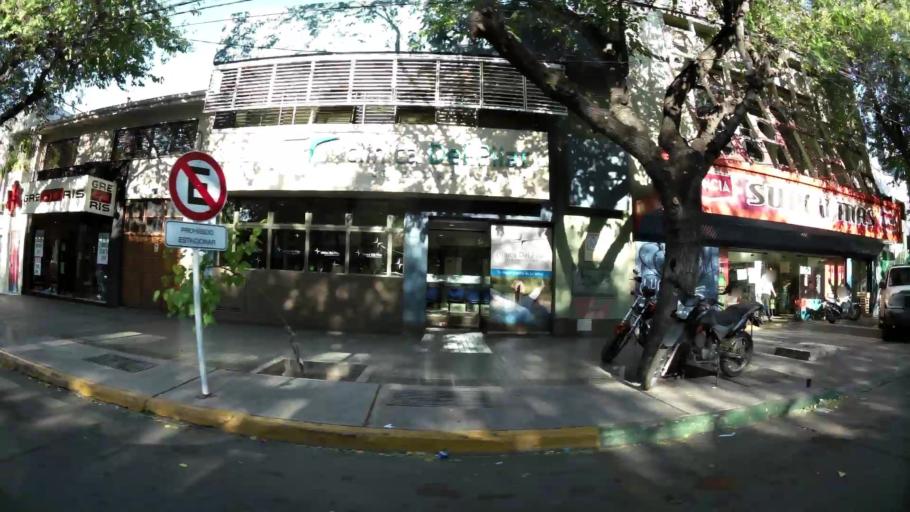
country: AR
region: Mendoza
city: Mendoza
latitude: -32.9057
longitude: -68.8433
